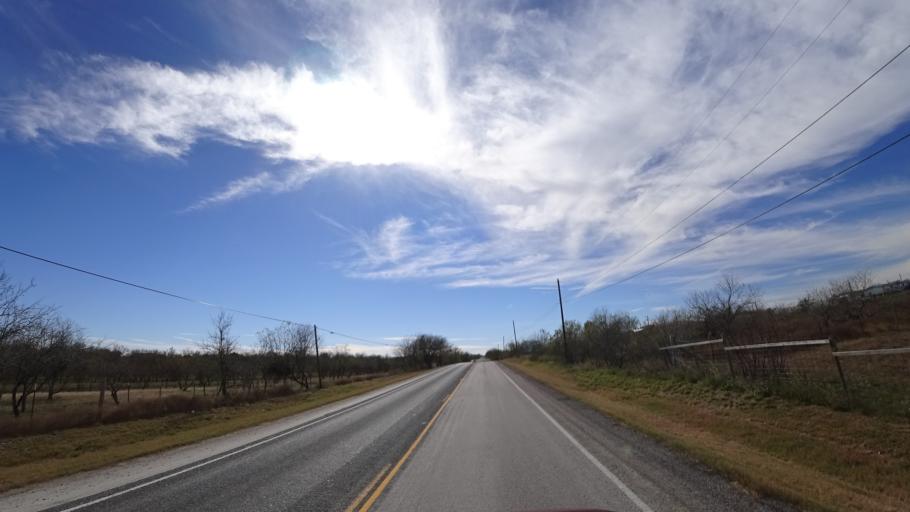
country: US
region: Texas
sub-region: Travis County
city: Onion Creek
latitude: 30.1175
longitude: -97.7173
